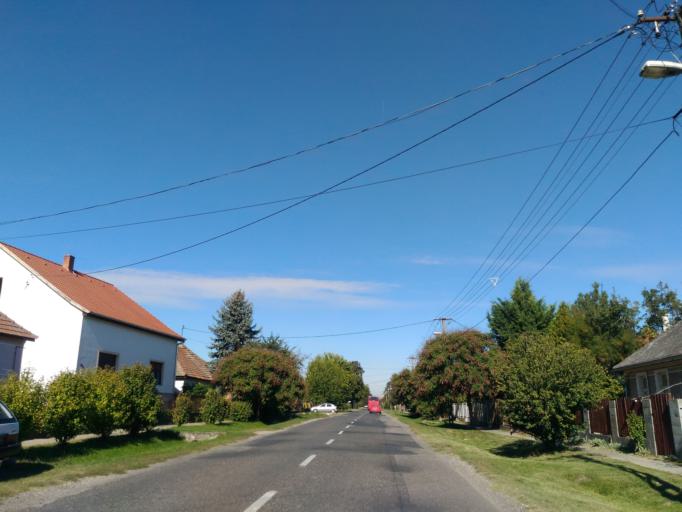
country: HU
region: Fejer
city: Ivancsa
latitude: 47.1459
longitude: 18.8327
